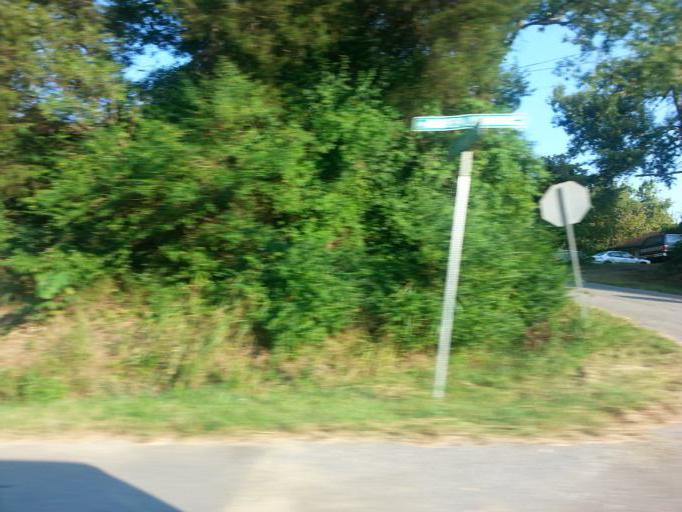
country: US
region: Tennessee
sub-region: Knox County
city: Mascot
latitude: 36.0417
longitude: -83.7167
